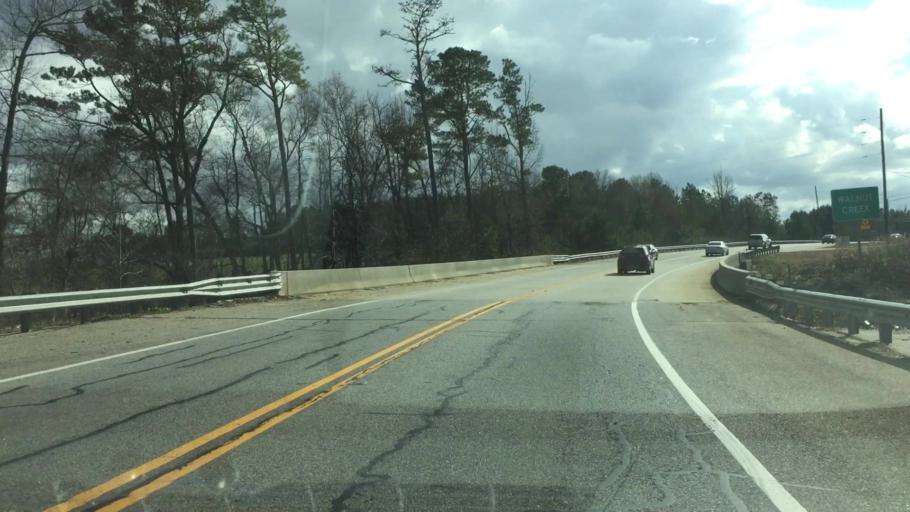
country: US
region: Georgia
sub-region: Henry County
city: McDonough
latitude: 33.4764
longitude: -84.1389
